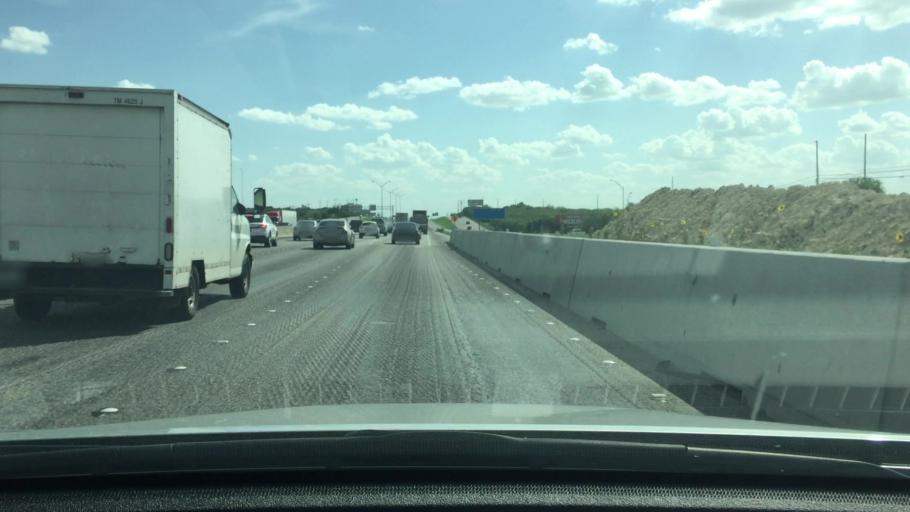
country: US
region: Texas
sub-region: Guadalupe County
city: Northcliff
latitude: 29.6237
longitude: -98.2395
